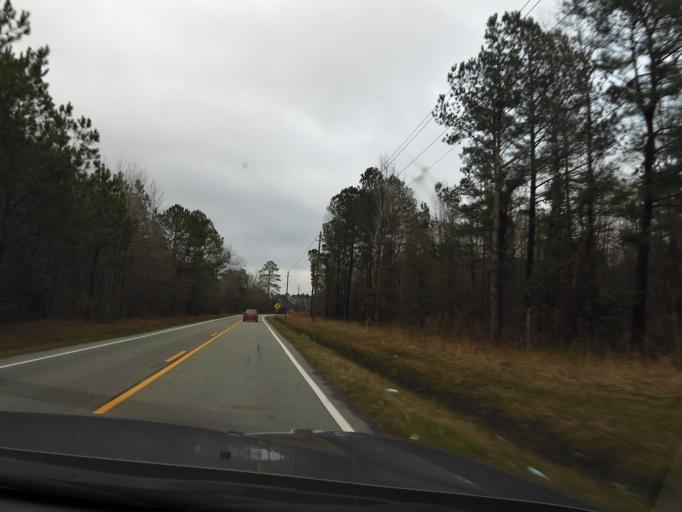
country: US
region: North Carolina
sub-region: Pitt County
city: Greenville
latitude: 35.6861
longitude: -77.3585
